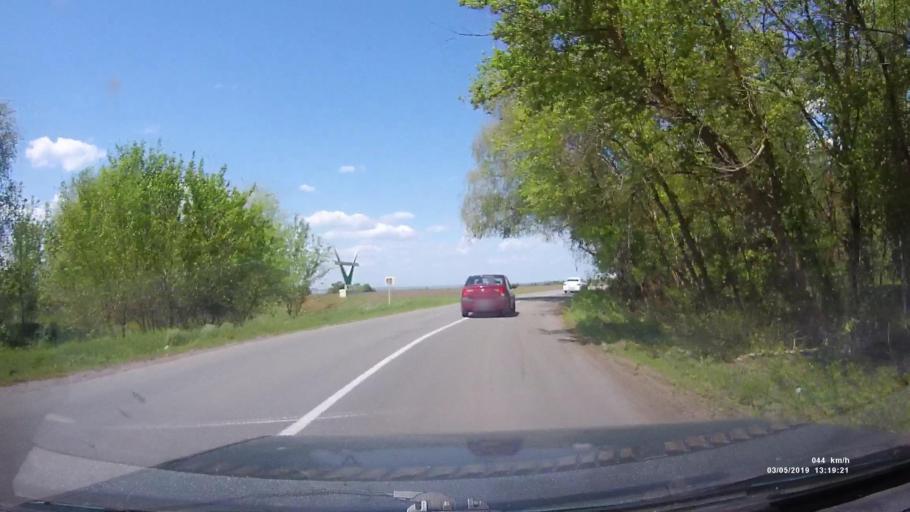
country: RU
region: Rostov
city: Semikarakorsk
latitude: 47.5370
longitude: 40.7477
